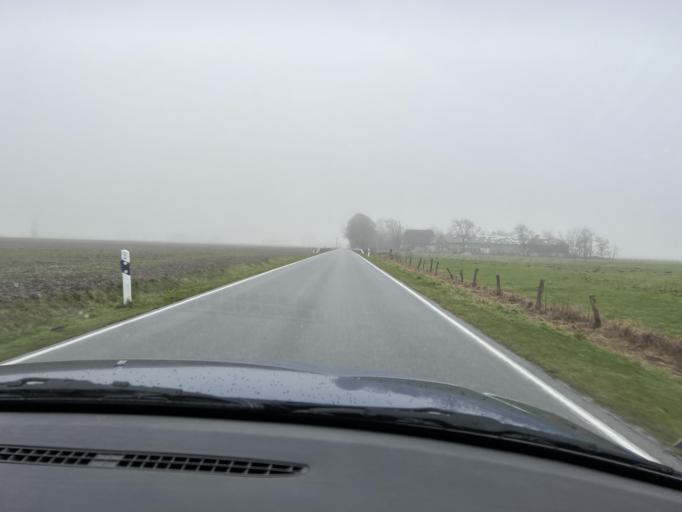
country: DE
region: Schleswig-Holstein
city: Wesselburenerkoog
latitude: 54.2477
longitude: 8.8932
